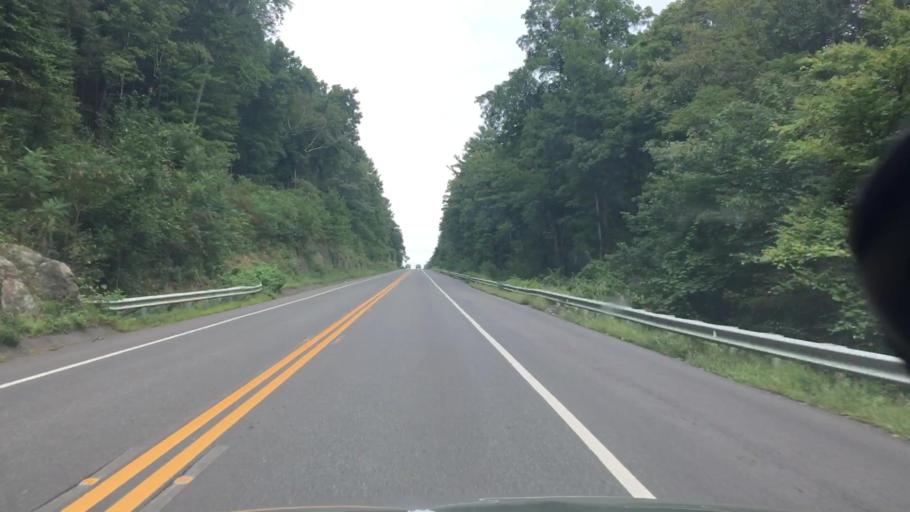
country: US
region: Massachusetts
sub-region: Franklin County
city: Greenfield
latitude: 42.6023
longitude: -72.6380
